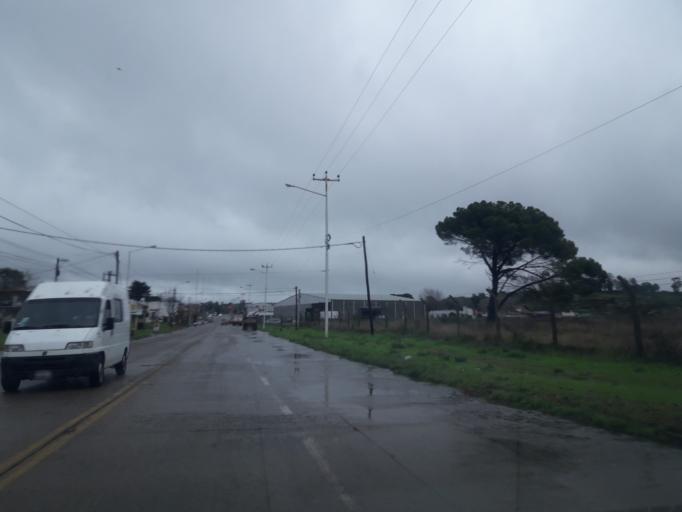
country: AR
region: Buenos Aires
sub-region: Partido de Tandil
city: Tandil
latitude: -37.3183
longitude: -59.1578
